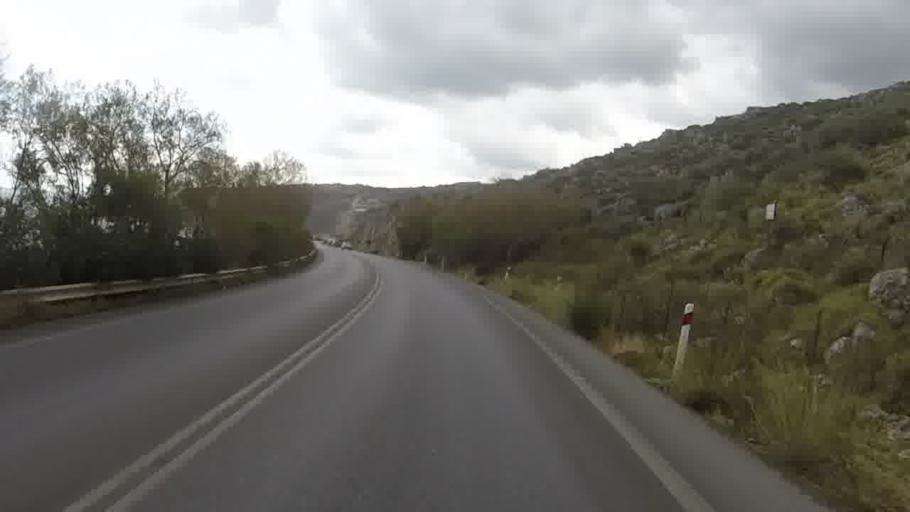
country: GR
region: Crete
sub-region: Nomos Rethymnis
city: Atsipopoulon
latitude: 35.3601
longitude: 24.3836
